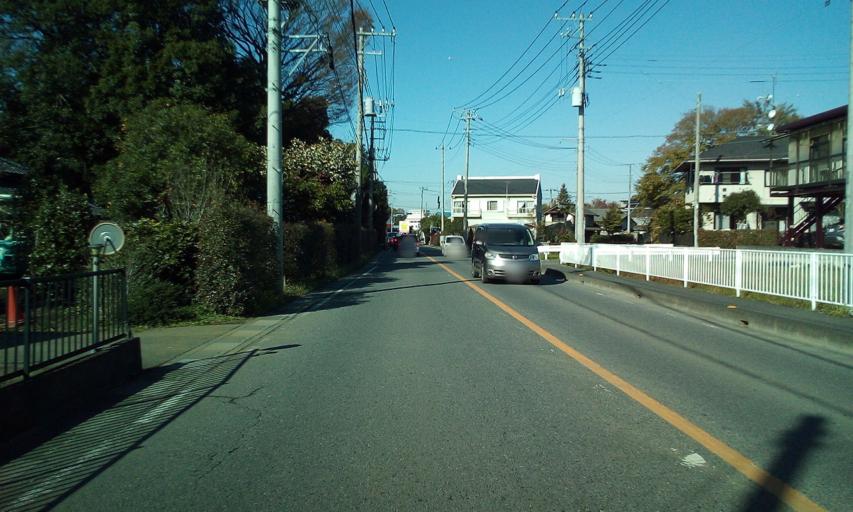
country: JP
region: Saitama
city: Kasukabe
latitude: 35.9802
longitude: 139.7981
